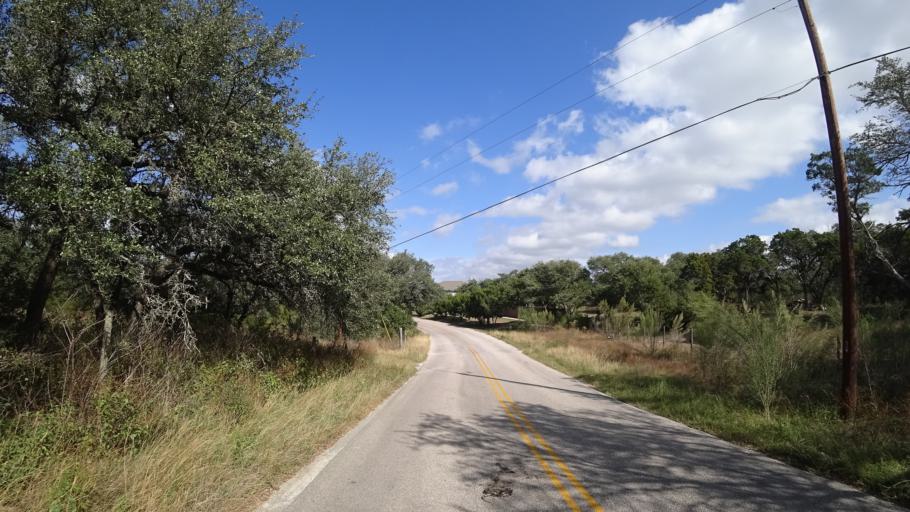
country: US
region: Texas
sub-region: Travis County
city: Bee Cave
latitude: 30.2482
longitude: -97.9315
